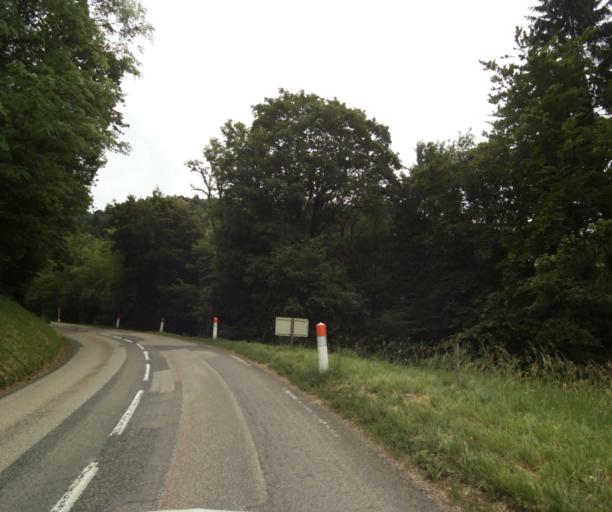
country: FR
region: Rhone-Alpes
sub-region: Departement de la Haute-Savoie
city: Perrignier
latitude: 46.2933
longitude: 6.4644
